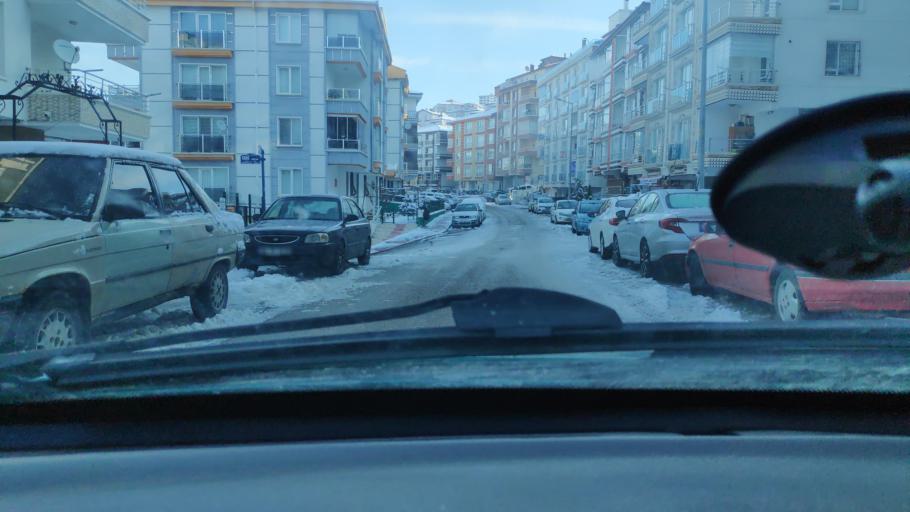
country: TR
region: Ankara
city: Ankara
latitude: 40.0111
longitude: 32.8436
